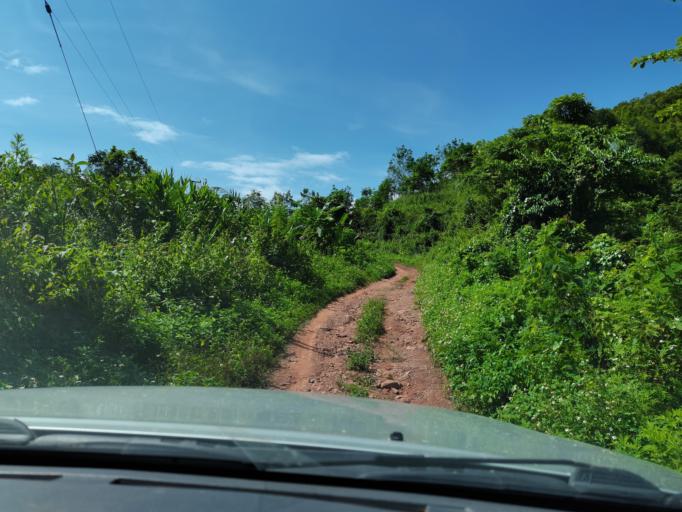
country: LA
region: Loungnamtha
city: Muang Nale
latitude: 20.5496
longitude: 101.0659
